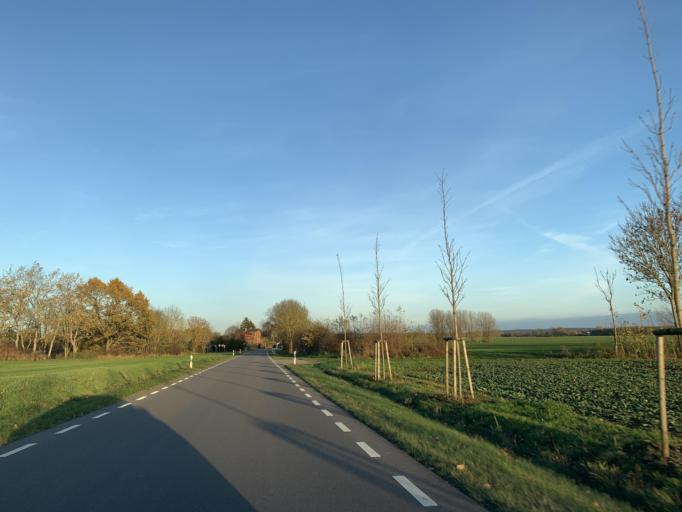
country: DE
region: Mecklenburg-Vorpommern
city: Blankensee
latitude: 53.4129
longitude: 13.3072
